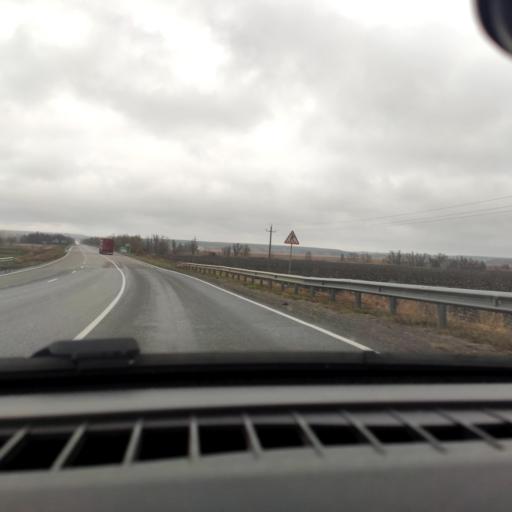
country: RU
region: Voronezj
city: Ostrogozhsk
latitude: 51.0274
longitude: 38.9873
